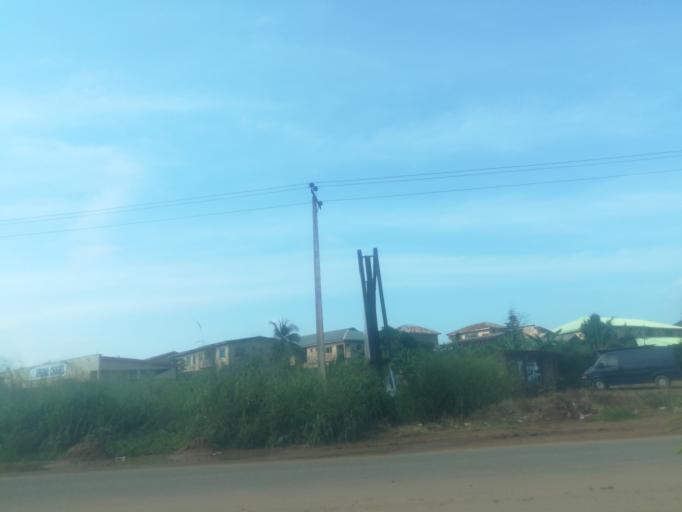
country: NG
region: Oyo
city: Ibadan
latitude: 7.3403
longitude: 3.8526
